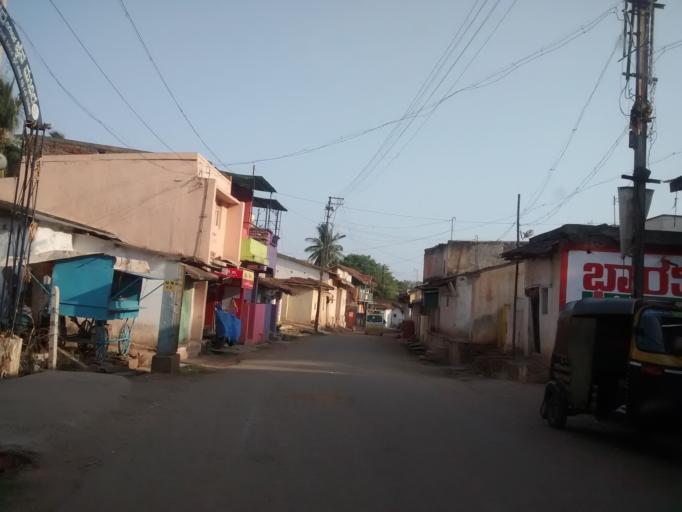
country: IN
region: Karnataka
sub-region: Dharwad
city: Hubli
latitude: 15.4541
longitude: 75.0184
